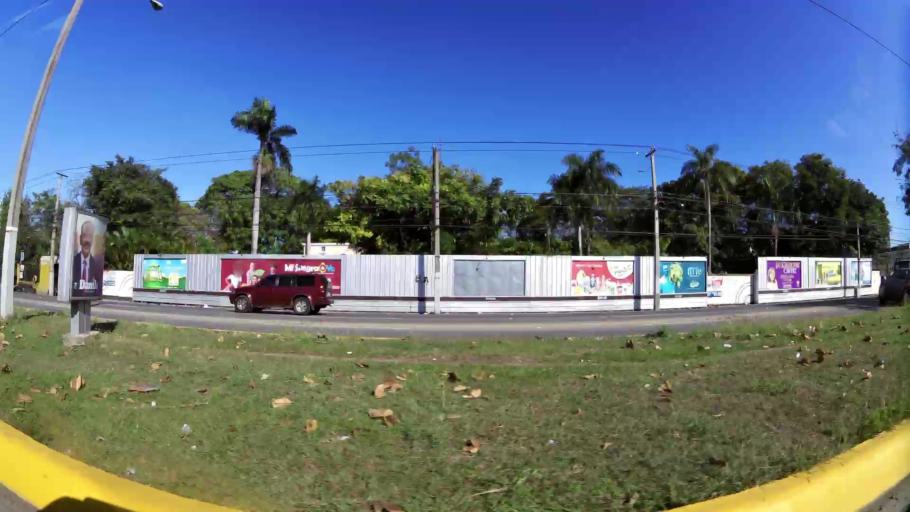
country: DO
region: Nacional
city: Bella Vista
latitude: 18.4574
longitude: -69.9708
